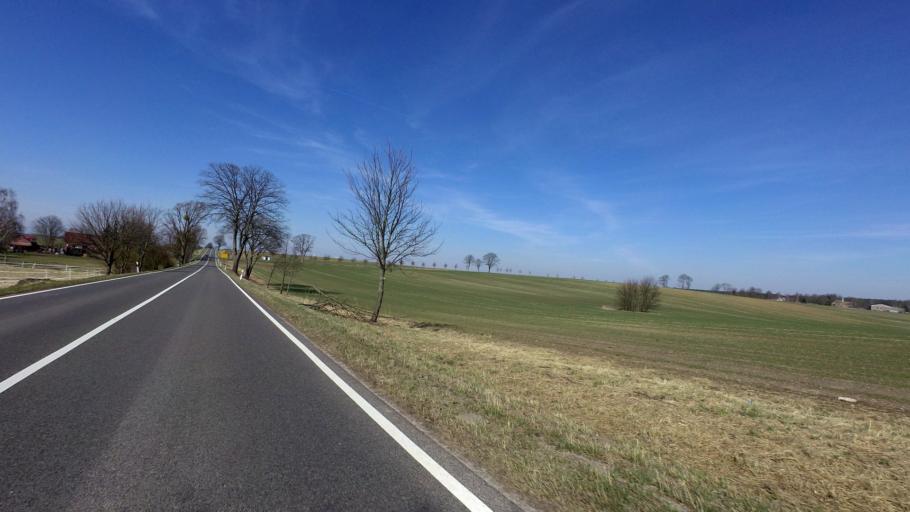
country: DE
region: Brandenburg
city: Protzel
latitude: 52.6025
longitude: 14.0239
